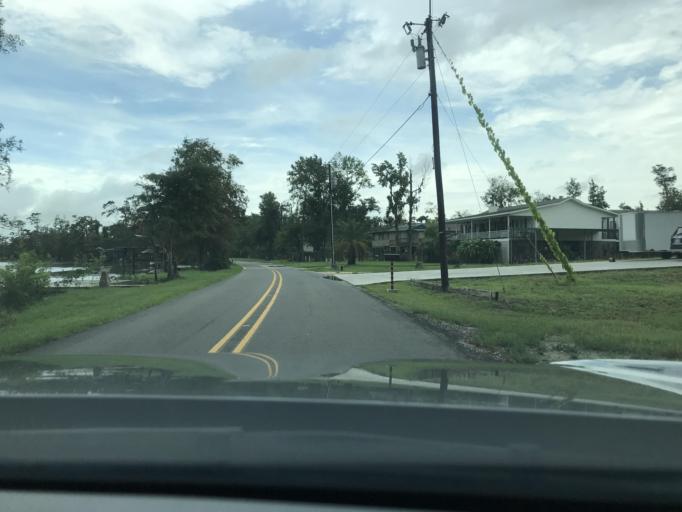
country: US
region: Louisiana
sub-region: Calcasieu Parish
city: Moss Bluff
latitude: 30.2805
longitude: -93.2285
